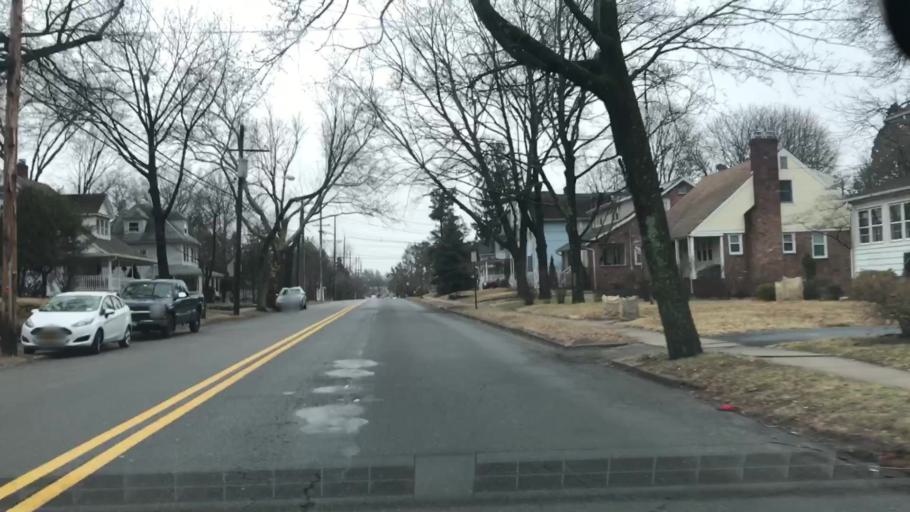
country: US
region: New Jersey
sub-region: Bergen County
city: Westwood
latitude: 40.9968
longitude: -74.0323
